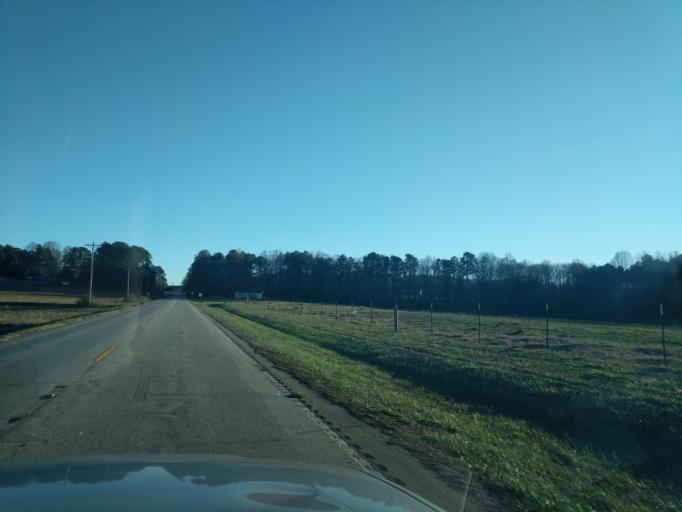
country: US
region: South Carolina
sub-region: Oconee County
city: Westminster
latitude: 34.6336
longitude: -83.0594
